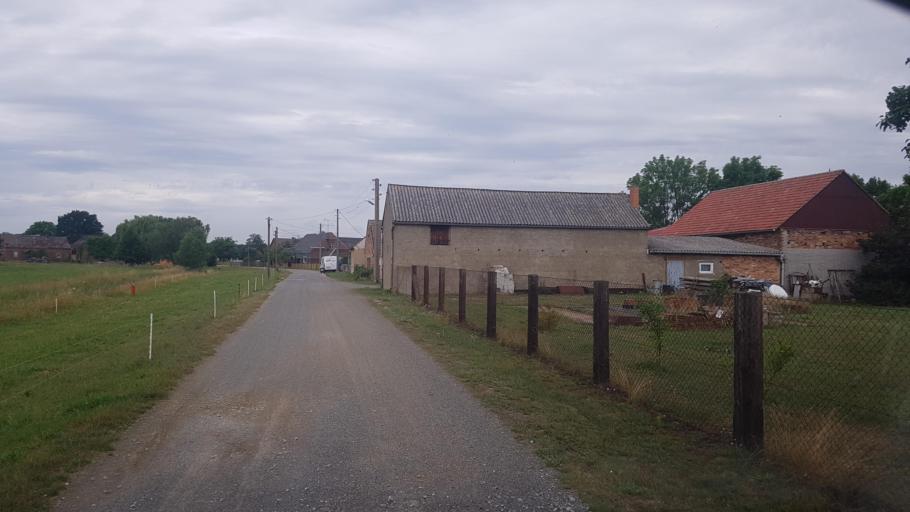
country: DE
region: Brandenburg
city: Crinitz
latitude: 51.7351
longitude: 13.8349
